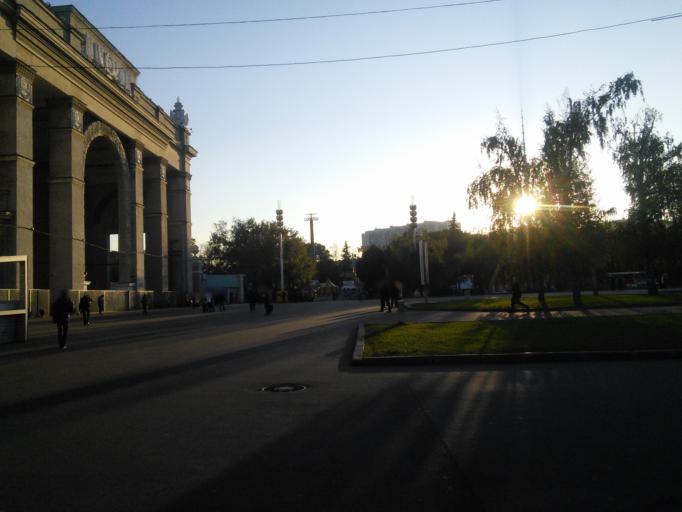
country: RU
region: Moscow
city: Ostankinskiy
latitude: 55.8269
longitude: 37.6380
